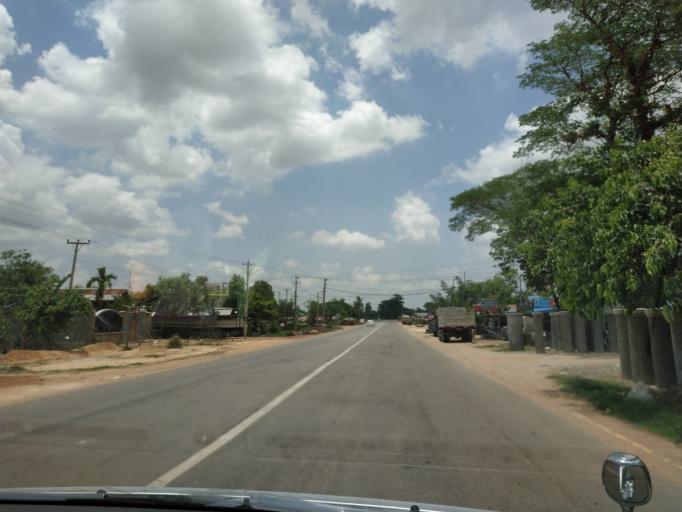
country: MM
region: Bago
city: Bago
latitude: 17.4734
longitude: 96.5387
